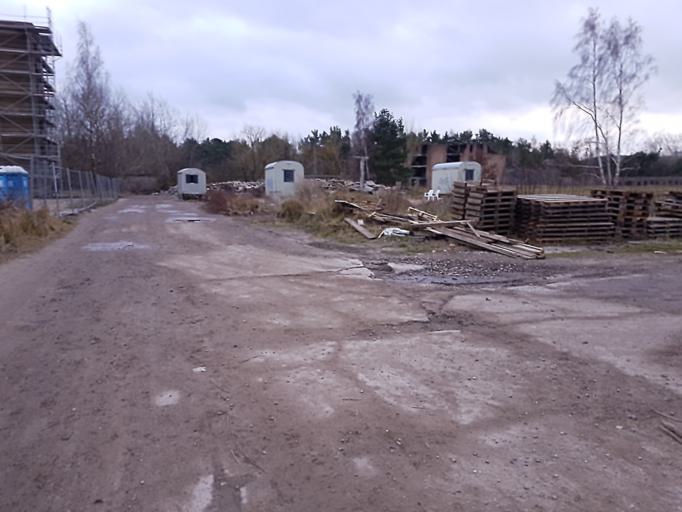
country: DE
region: Mecklenburg-Vorpommern
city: Ostseebad Binz
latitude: 54.4439
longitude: 13.5724
